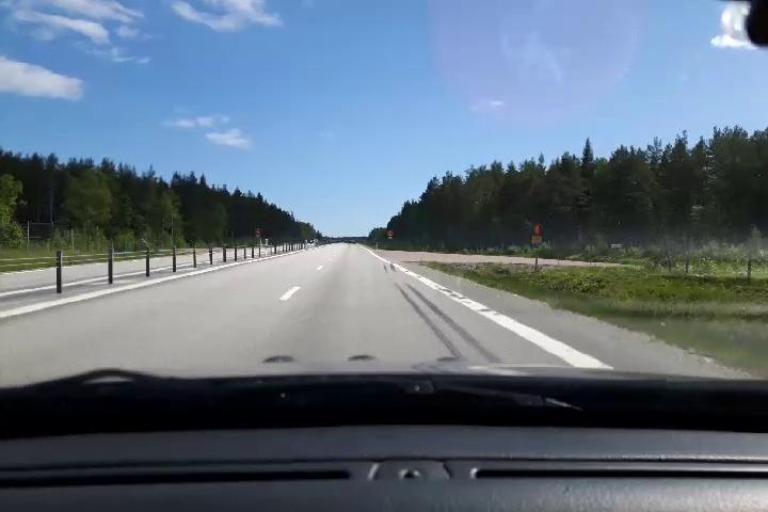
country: SE
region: Gaevleborg
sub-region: Hudiksvalls Kommun
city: Hudiksvall
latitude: 61.7076
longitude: 17.0500
